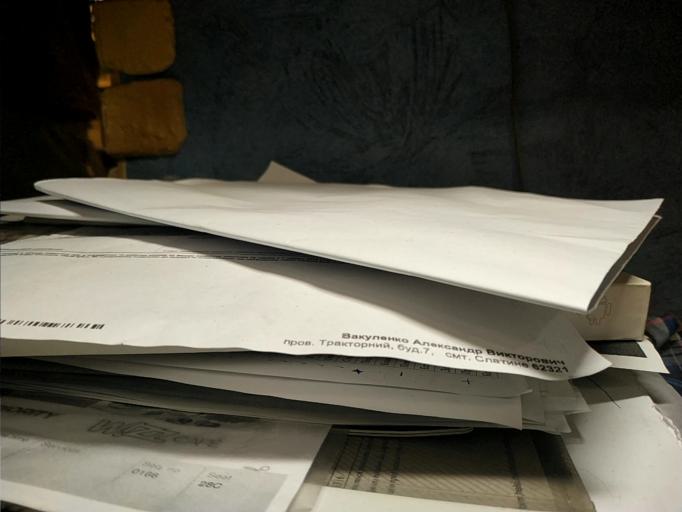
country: RU
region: Tverskaya
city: Zubtsov
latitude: 56.1006
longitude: 34.6855
